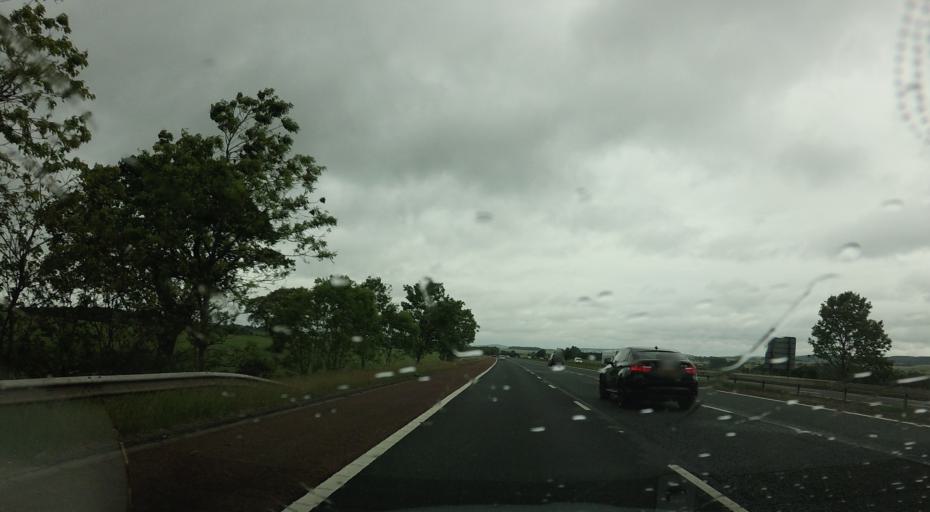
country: GB
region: England
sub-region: Cumbria
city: Penrith
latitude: 54.7046
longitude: -2.7924
